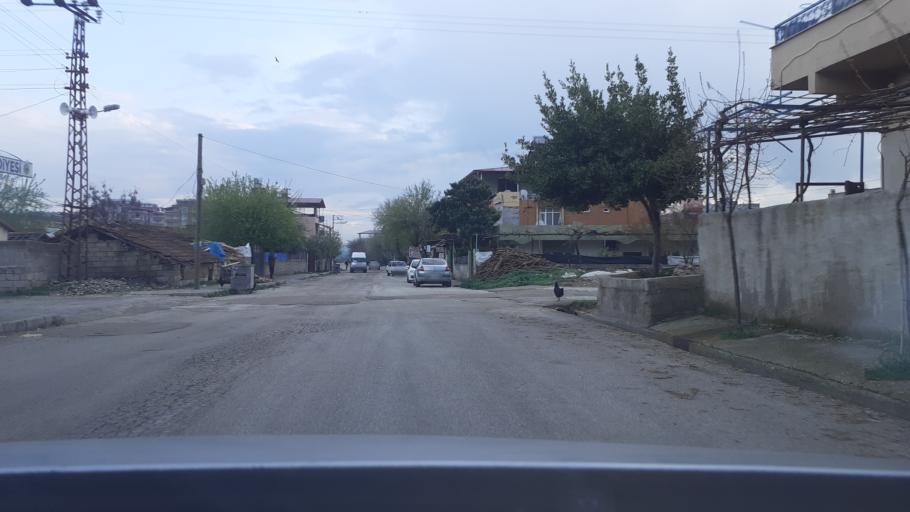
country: TR
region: Hatay
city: Kirikhan
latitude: 36.4843
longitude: 36.3502
